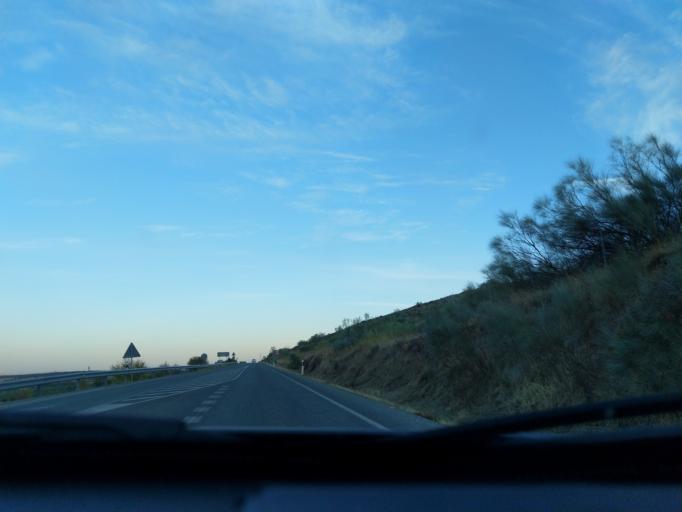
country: ES
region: Extremadura
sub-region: Provincia de Badajoz
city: Casas de Reina
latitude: 38.1951
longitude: -5.9554
